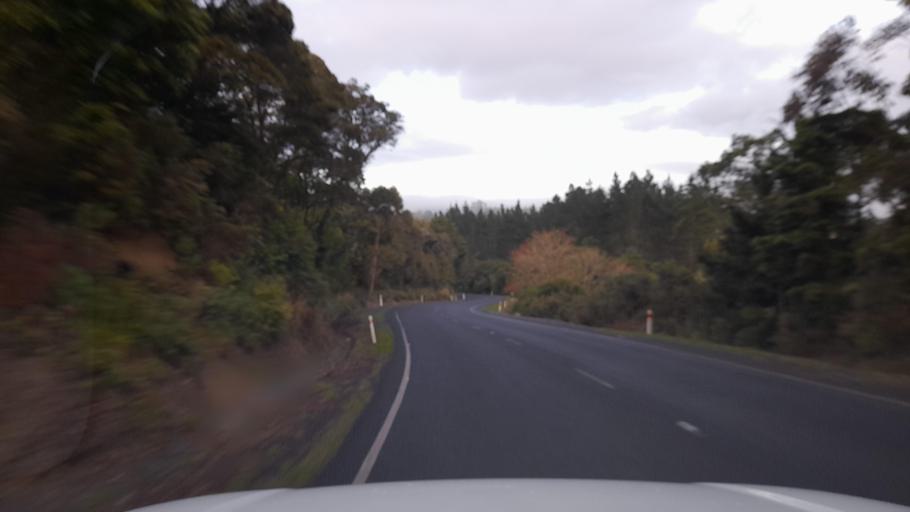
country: NZ
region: Northland
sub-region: Kaipara District
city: Dargaville
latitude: -35.7116
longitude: 173.9629
